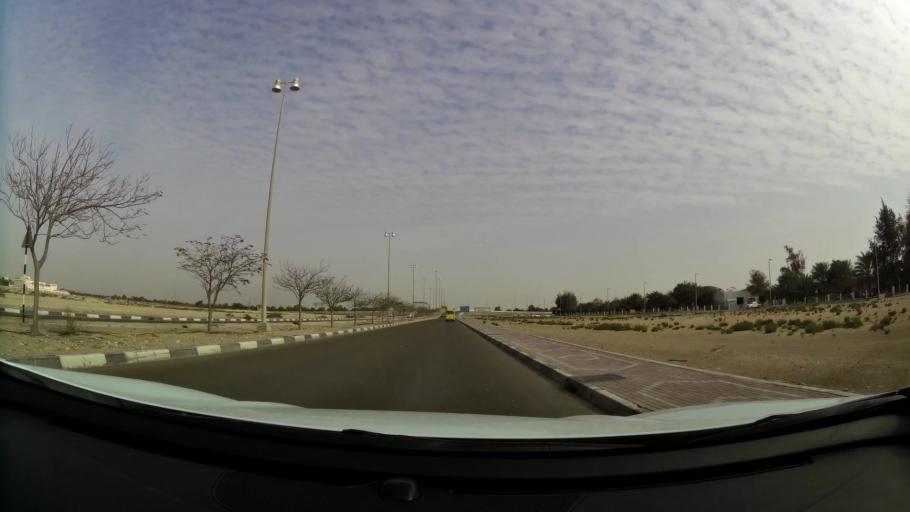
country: AE
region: Abu Dhabi
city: Abu Dhabi
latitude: 24.6235
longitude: 54.7112
